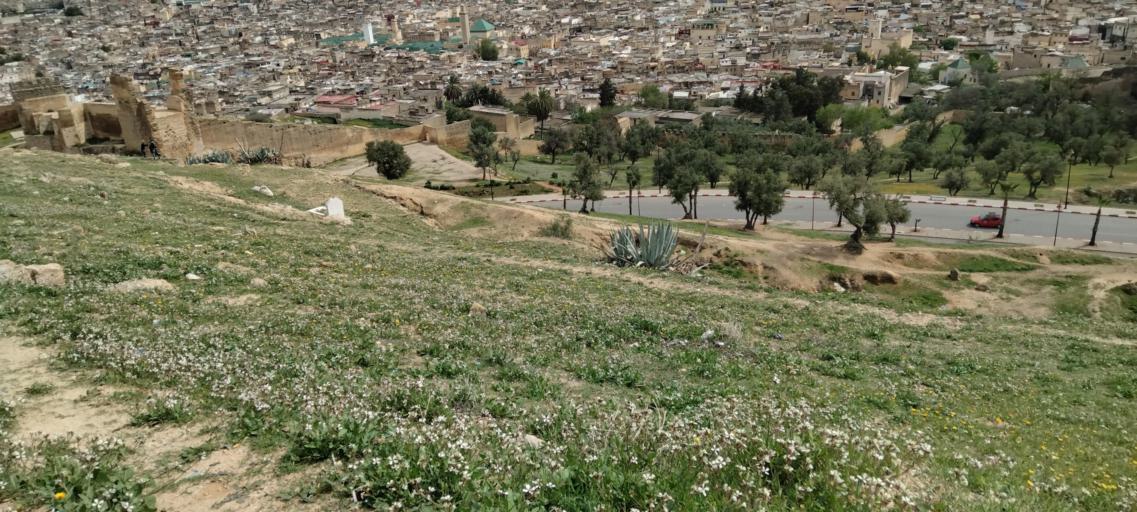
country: MA
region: Fes-Boulemane
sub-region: Fes
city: Fes
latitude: 34.0697
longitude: -4.9795
